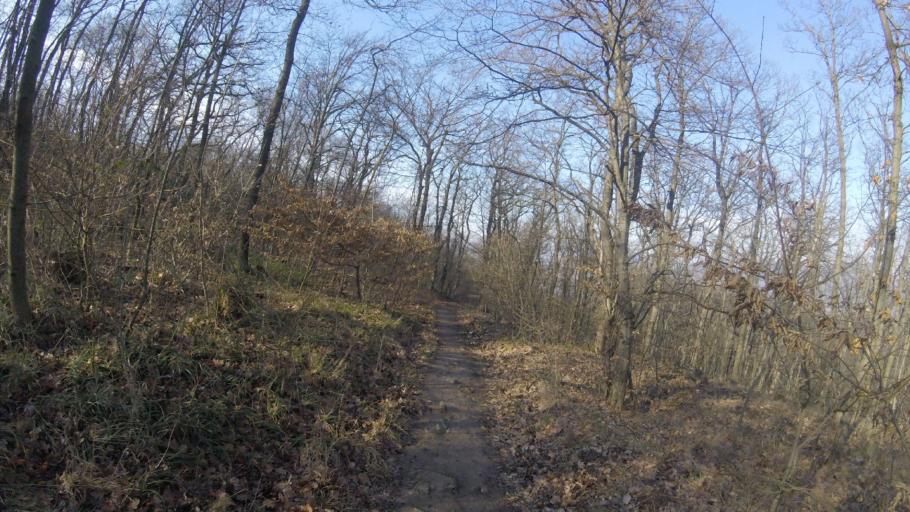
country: HU
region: Pest
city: Csobanka
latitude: 47.6420
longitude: 18.9767
